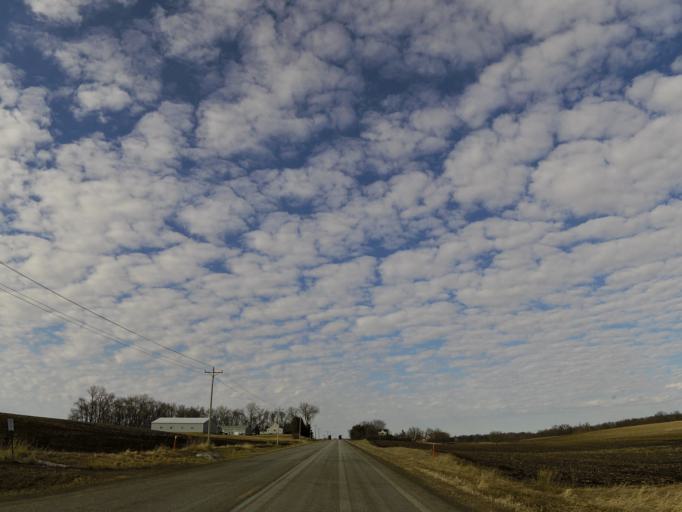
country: US
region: Minnesota
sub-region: Le Sueur County
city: New Prague
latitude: 44.5794
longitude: -93.5576
